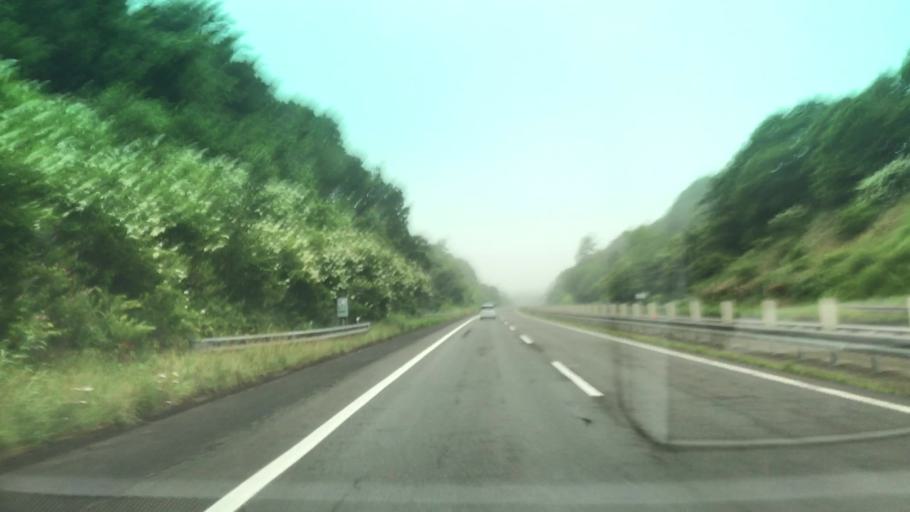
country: JP
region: Hokkaido
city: Muroran
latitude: 42.4350
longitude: 141.1251
